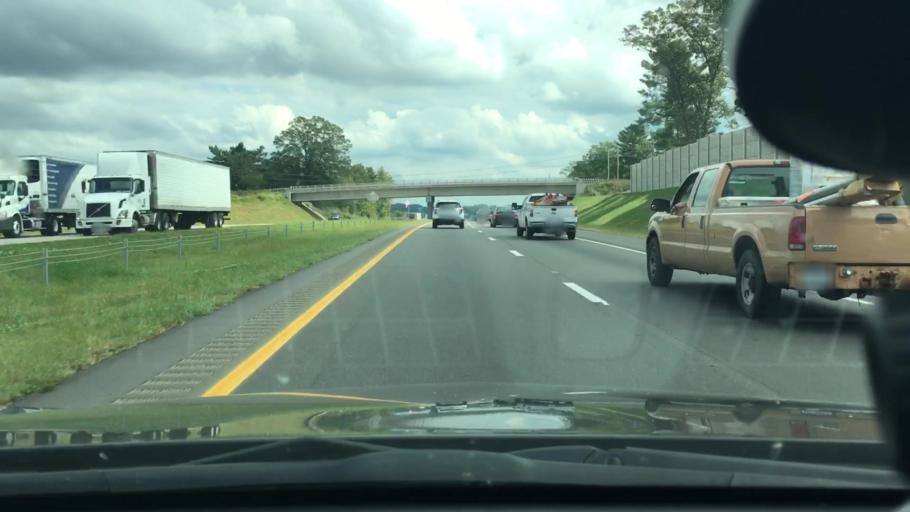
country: US
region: North Carolina
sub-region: Iredell County
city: Statesville
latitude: 35.8048
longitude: -80.8923
